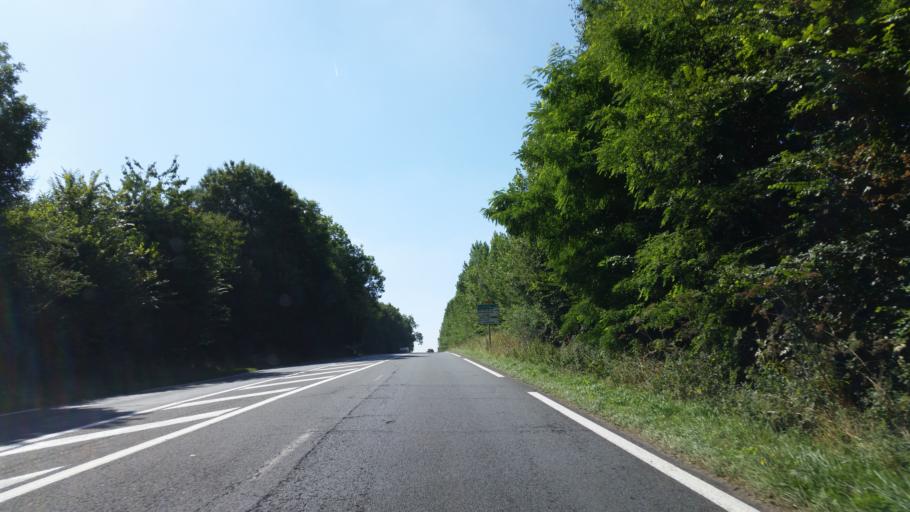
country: FR
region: Lower Normandy
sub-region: Departement du Calvados
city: Saint-Gatien-des-Bois
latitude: 49.2780
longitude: 0.2153
